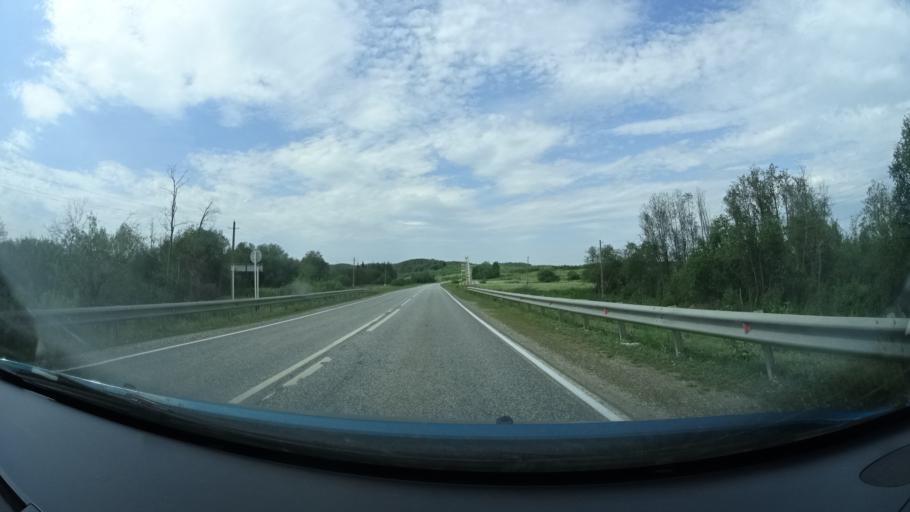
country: RU
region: Perm
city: Osa
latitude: 57.1060
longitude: 55.5254
